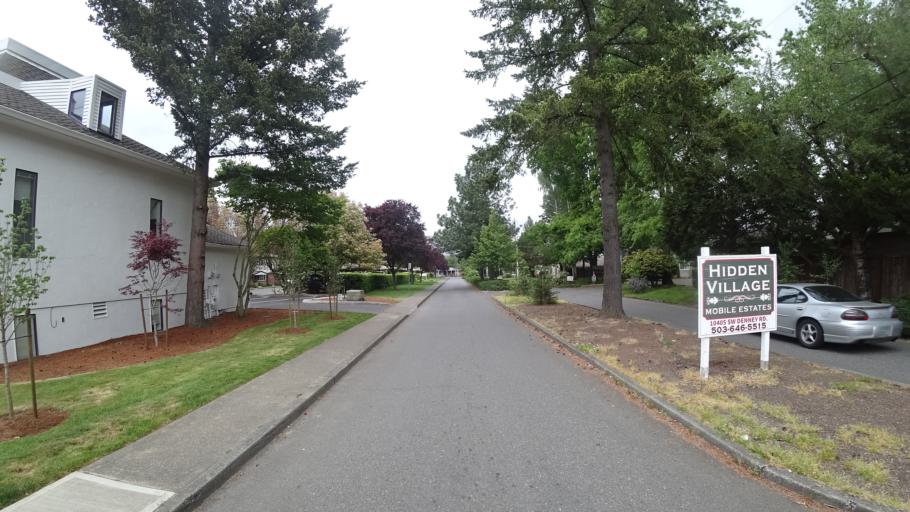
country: US
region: Oregon
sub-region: Washington County
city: Raleigh Hills
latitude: 45.4695
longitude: -122.7839
